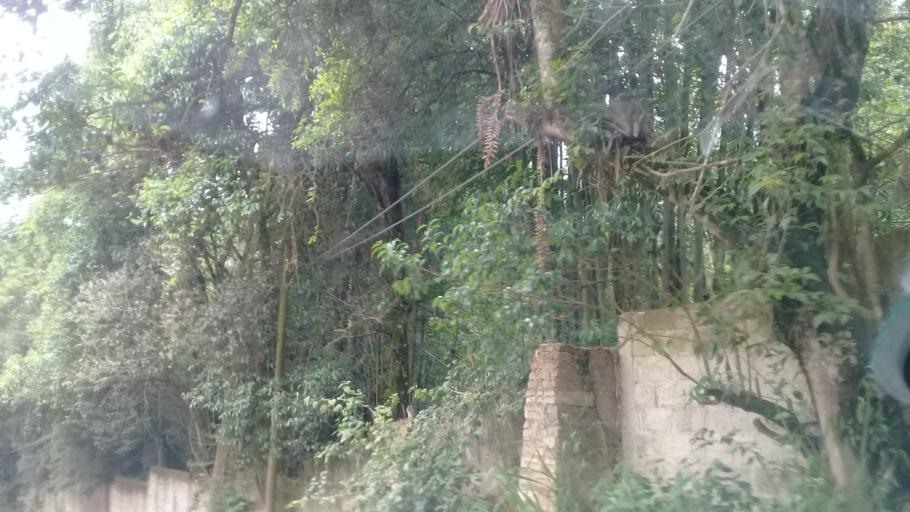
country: MX
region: Veracruz
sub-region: Emiliano Zapata
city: Las Trancas
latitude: 19.4988
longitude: -96.8704
